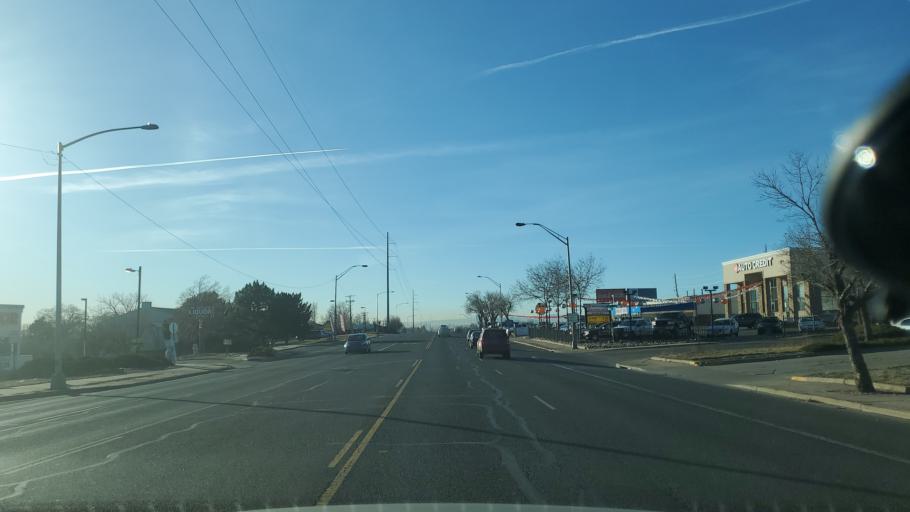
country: US
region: Colorado
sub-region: Adams County
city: Thornton
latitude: 39.8531
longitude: -104.9779
